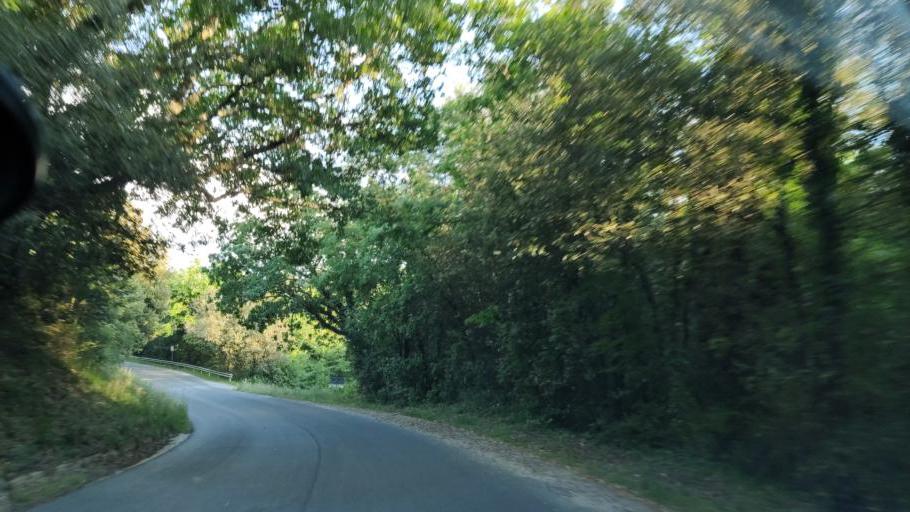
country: IT
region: Umbria
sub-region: Provincia di Terni
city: Lugnano in Teverina
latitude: 42.5878
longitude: 12.3773
